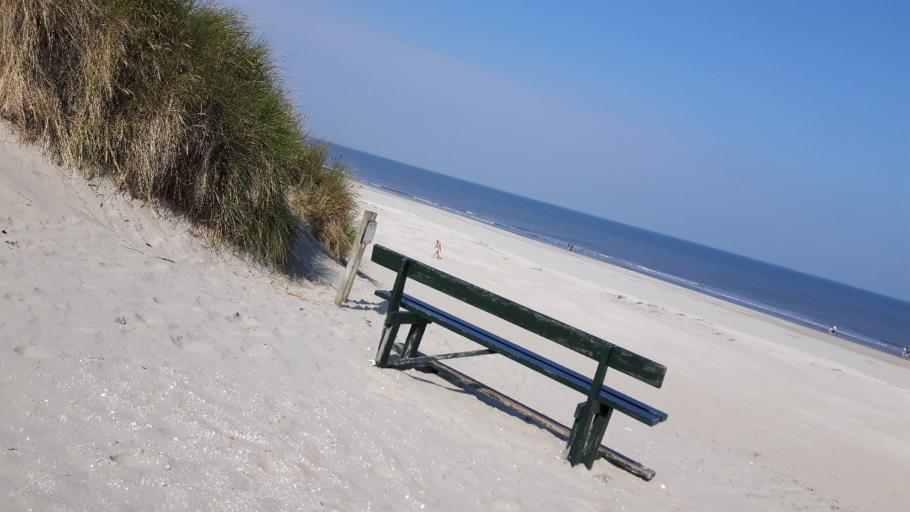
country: NL
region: Friesland
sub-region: Gemeente Ameland
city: Nes
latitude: 53.4620
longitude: 5.8176
